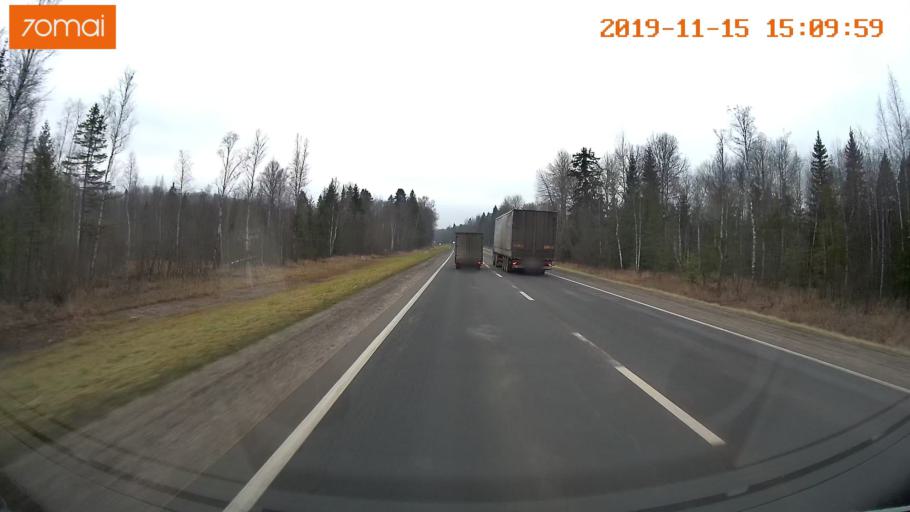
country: RU
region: Jaroslavl
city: Prechistoye
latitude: 58.3525
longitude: 40.2588
